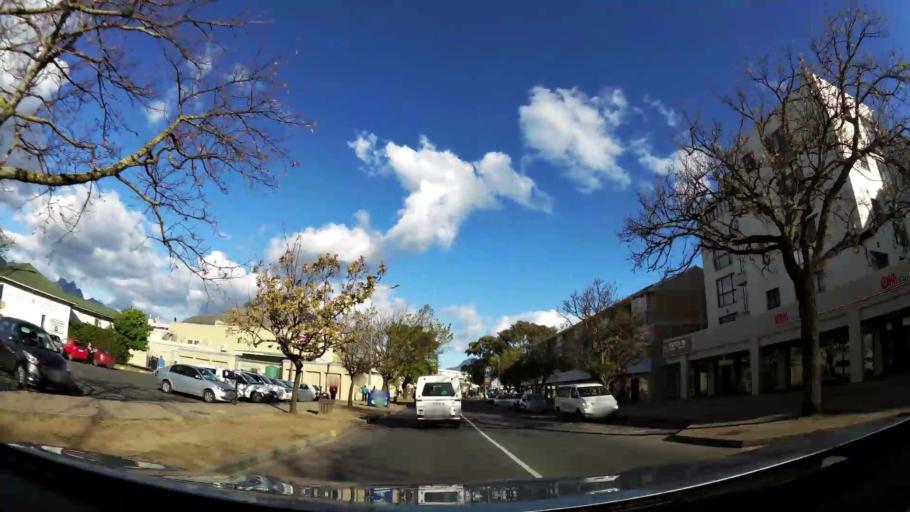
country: ZA
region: Western Cape
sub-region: Cape Winelands District Municipality
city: Stellenbosch
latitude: -33.9310
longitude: 18.8579
